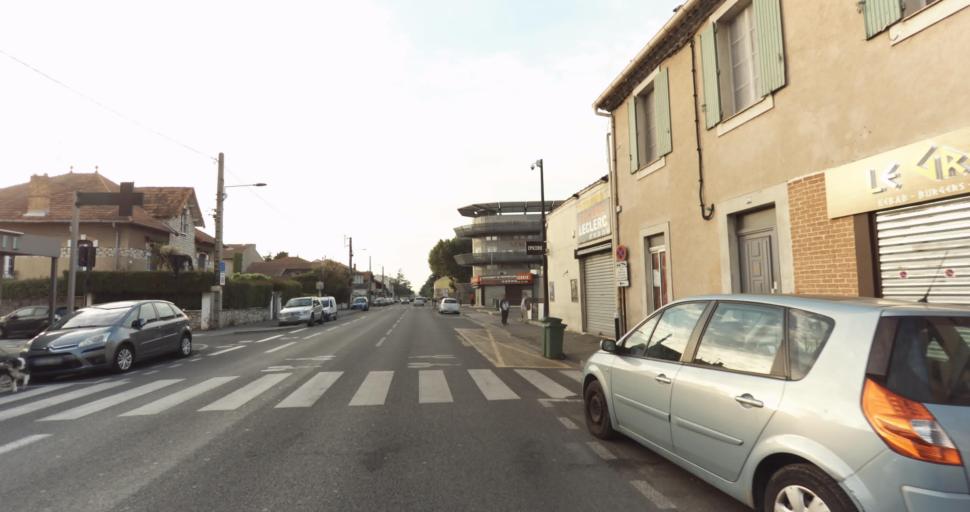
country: FR
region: Languedoc-Roussillon
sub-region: Departement du Gard
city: Nimes
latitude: 43.8287
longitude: 4.3725
